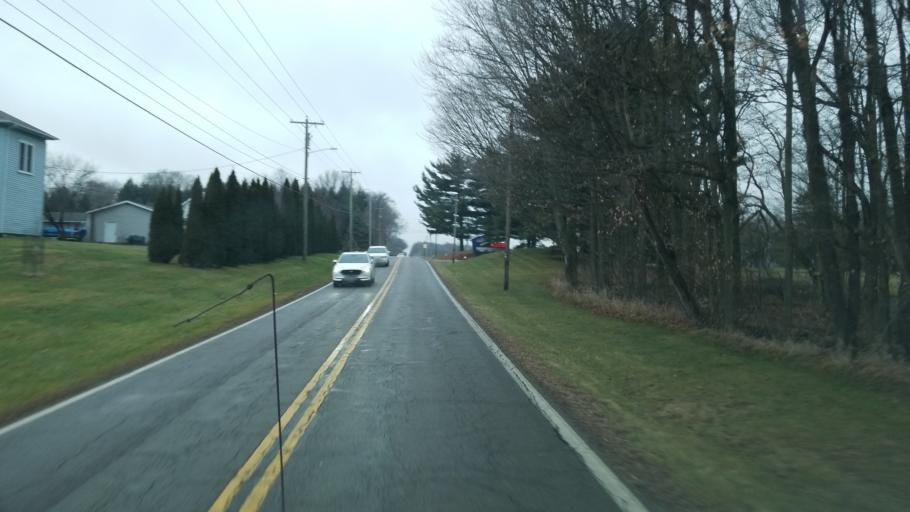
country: US
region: Ohio
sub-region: Wayne County
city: Orrville
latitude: 40.8592
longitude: -81.7889
